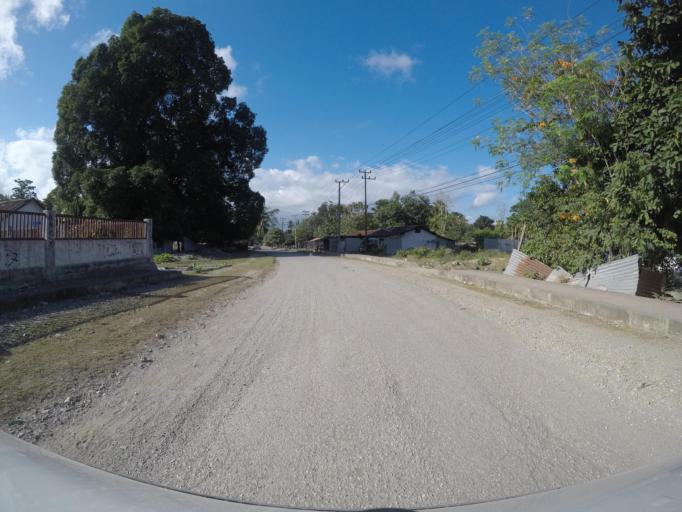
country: TL
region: Viqueque
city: Viqueque
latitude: -8.8531
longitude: 126.3657
